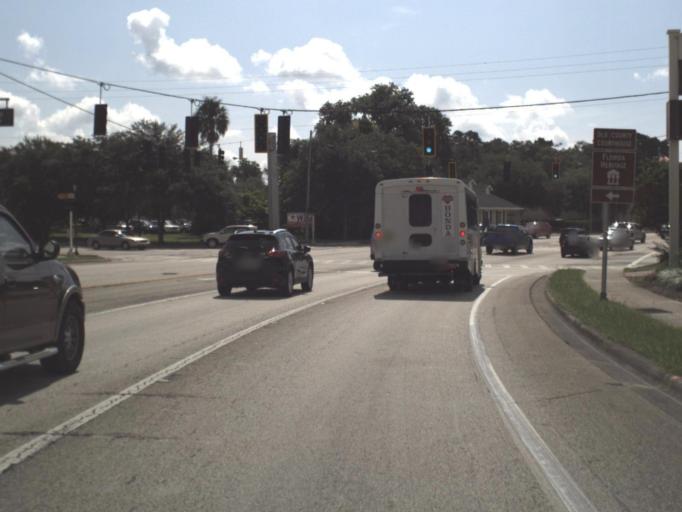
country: US
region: Florida
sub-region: Citrus County
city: Inverness
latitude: 28.8354
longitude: -82.3308
